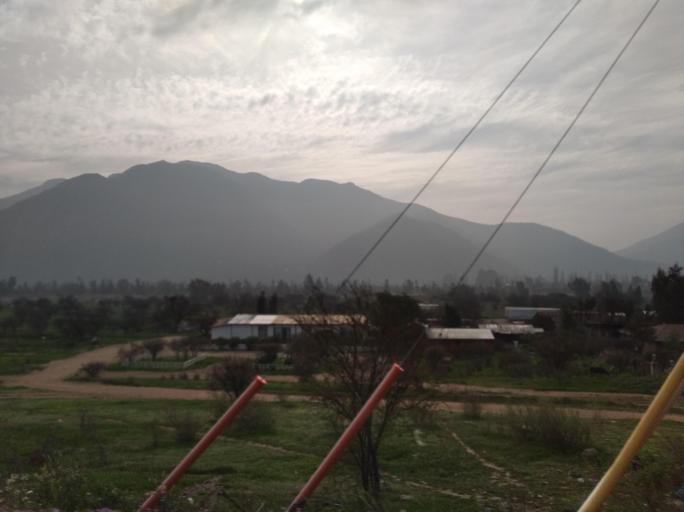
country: CL
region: Santiago Metropolitan
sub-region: Provincia de Chacabuco
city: Lampa
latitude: -33.2575
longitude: -70.9028
